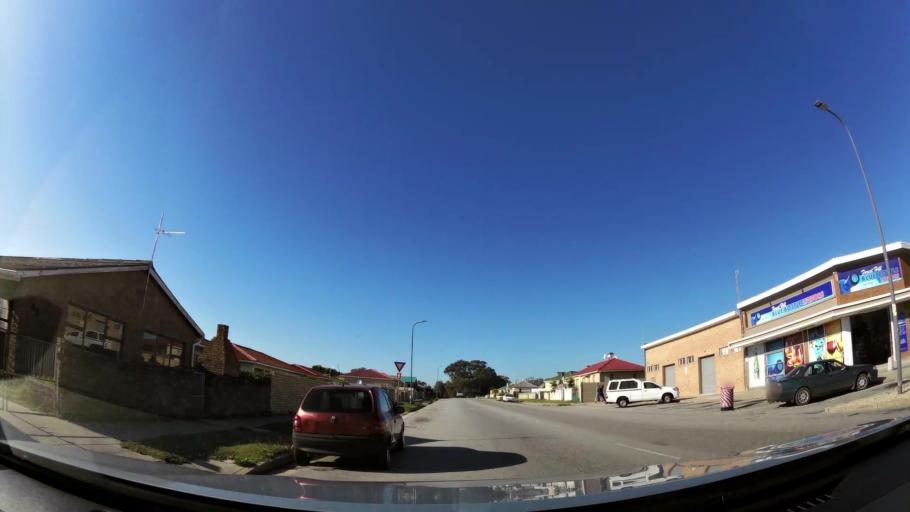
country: ZA
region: Eastern Cape
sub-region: Nelson Mandela Bay Metropolitan Municipality
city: Port Elizabeth
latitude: -33.9829
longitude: 25.6312
